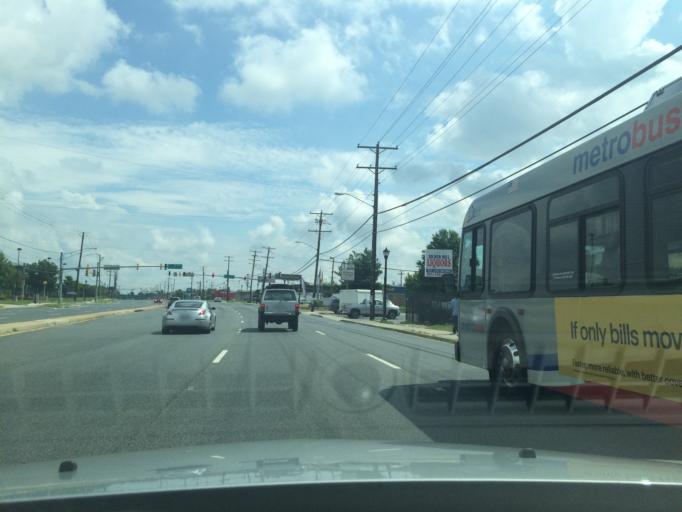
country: US
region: Maryland
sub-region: Prince George's County
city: Suitland
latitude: 38.8439
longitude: -76.9294
